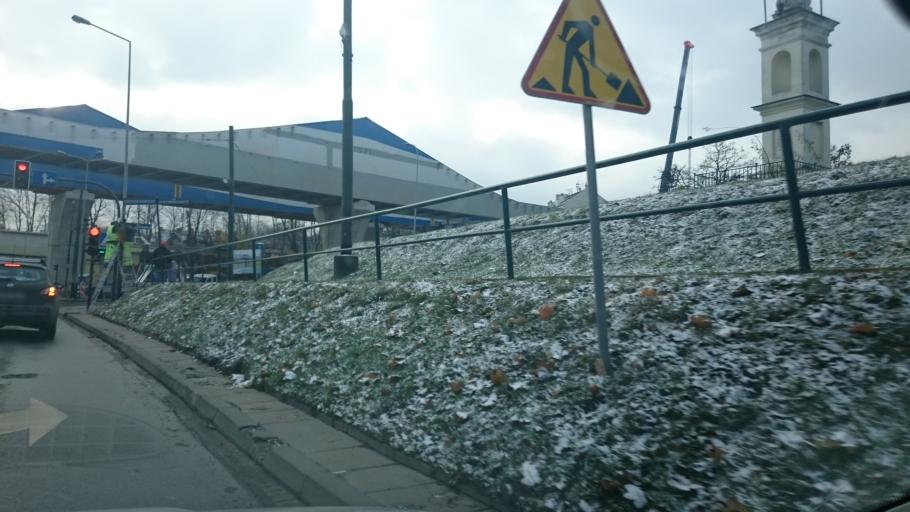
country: PL
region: Lesser Poland Voivodeship
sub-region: Krakow
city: Krakow
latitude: 50.0425
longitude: 19.9604
